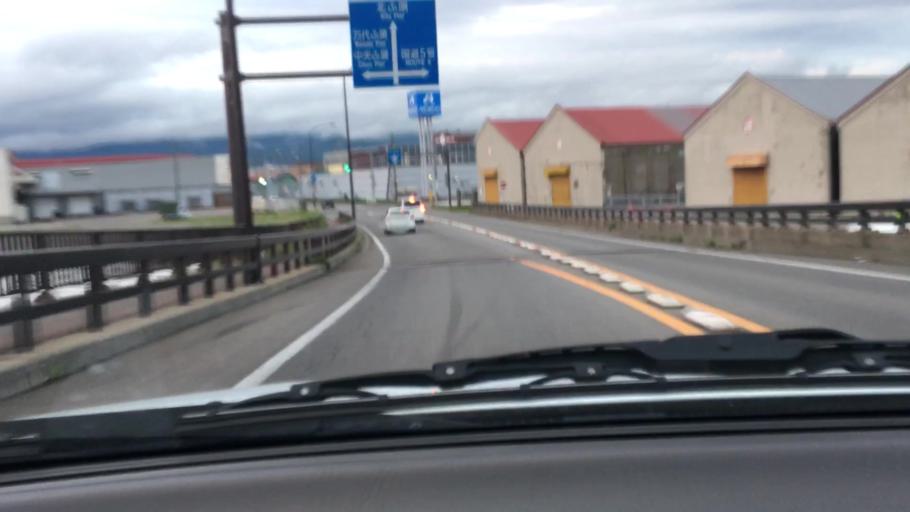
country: JP
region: Hokkaido
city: Hakodate
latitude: 41.7856
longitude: 140.7276
